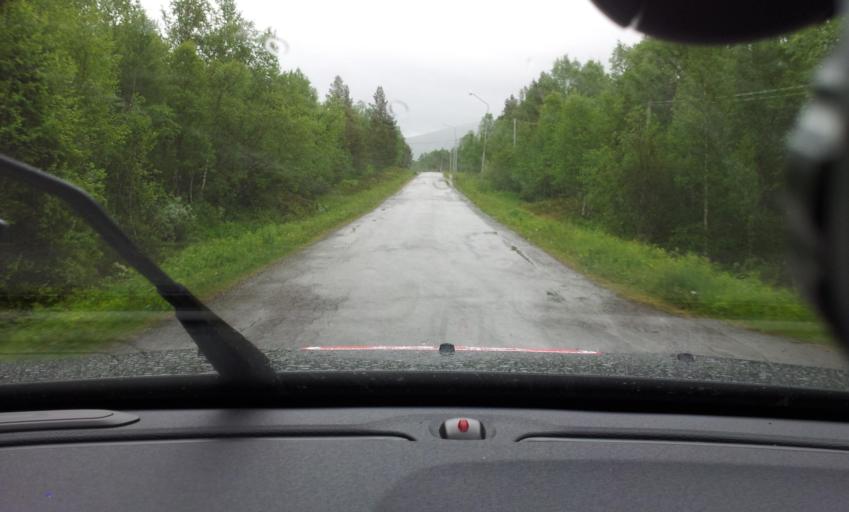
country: SE
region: Jaemtland
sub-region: Are Kommun
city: Are
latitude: 63.1481
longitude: 12.9527
